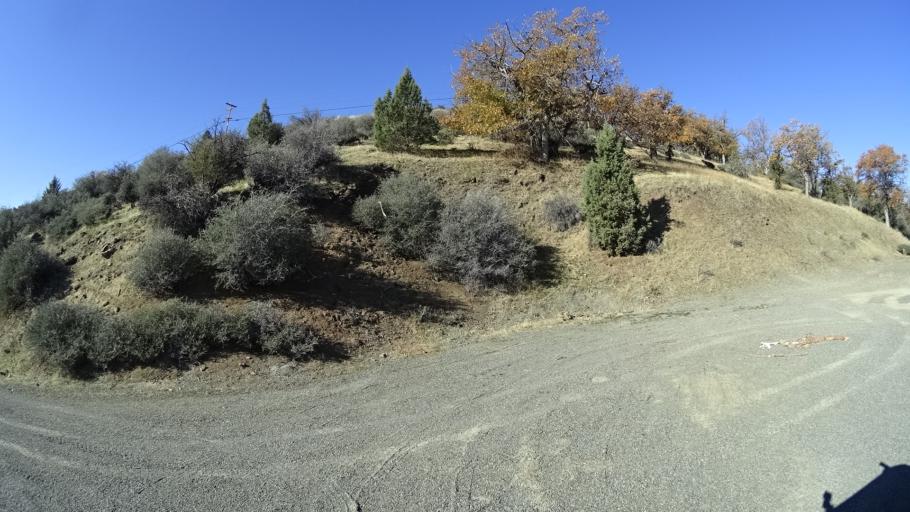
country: US
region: California
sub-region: Siskiyou County
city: Montague
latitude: 41.9761
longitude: -122.3009
